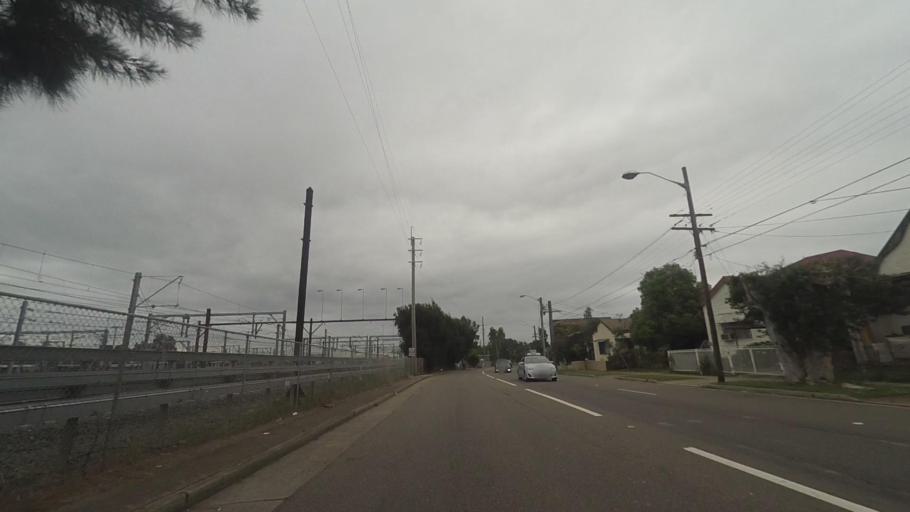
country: AU
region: New South Wales
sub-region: Auburn
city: Auburn
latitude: -33.8447
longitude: 151.0284
